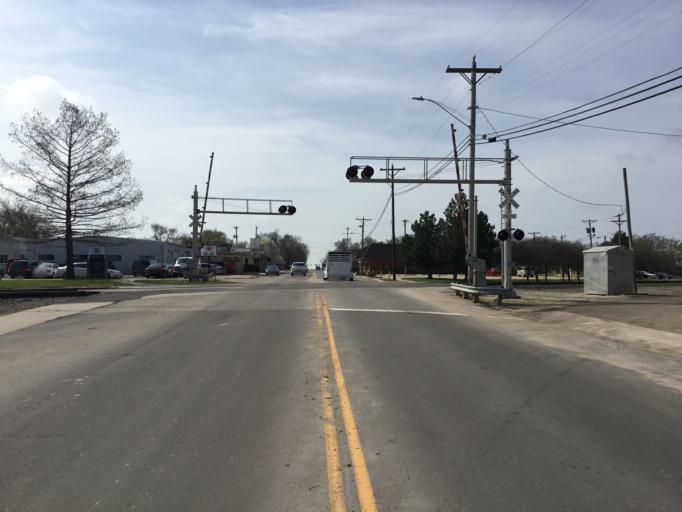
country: US
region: Kansas
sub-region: Butler County
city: Rose Hill
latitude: 37.5610
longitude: -97.1351
